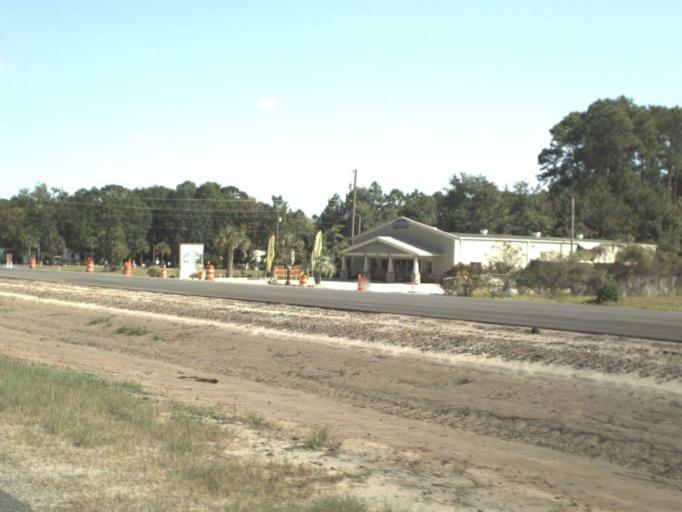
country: US
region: Florida
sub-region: Walton County
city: Freeport
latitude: 30.4541
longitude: -86.1314
